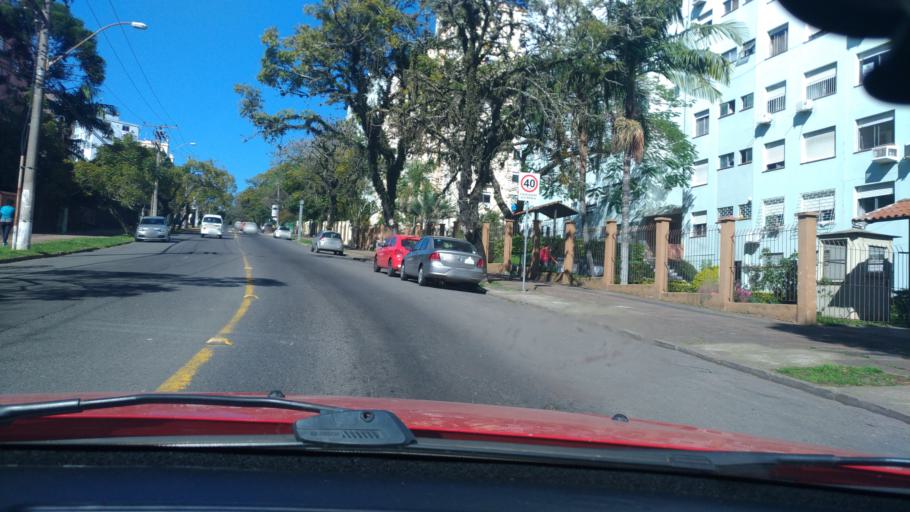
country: BR
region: Rio Grande do Sul
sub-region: Porto Alegre
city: Porto Alegre
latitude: -30.0387
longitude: -51.1451
